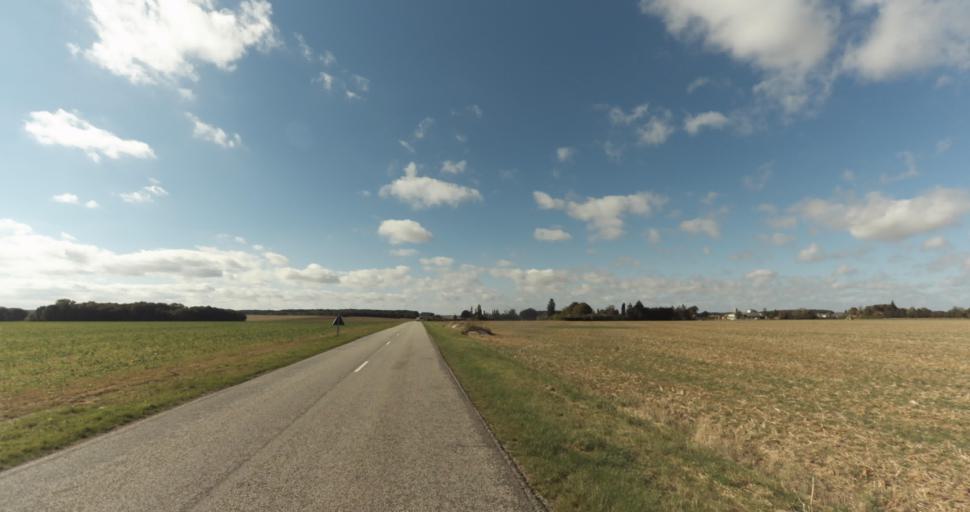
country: FR
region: Centre
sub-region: Departement d'Eure-et-Loir
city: Treon
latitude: 48.7023
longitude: 1.2947
